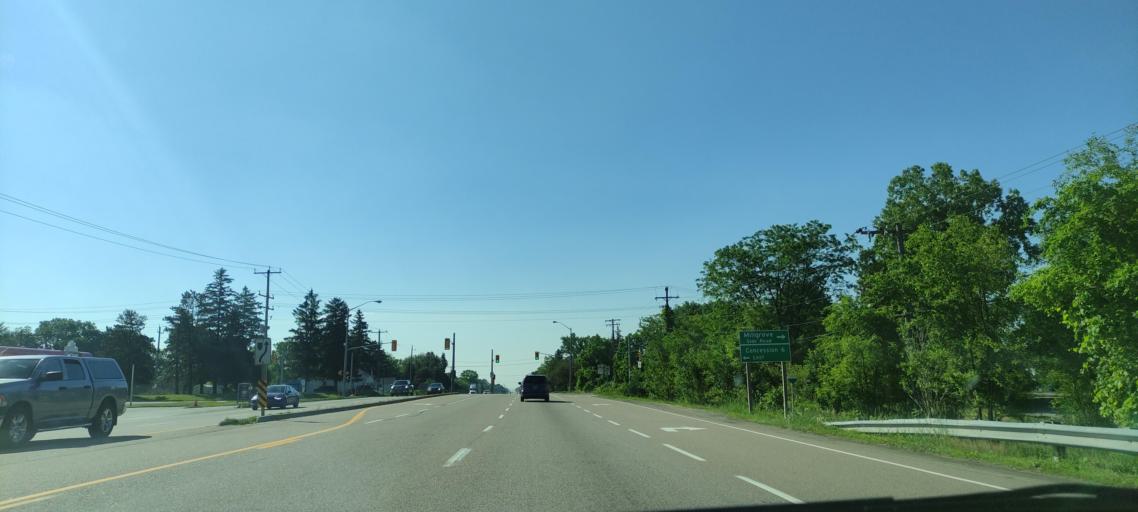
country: CA
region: Ontario
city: Ancaster
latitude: 43.3431
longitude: -79.9603
